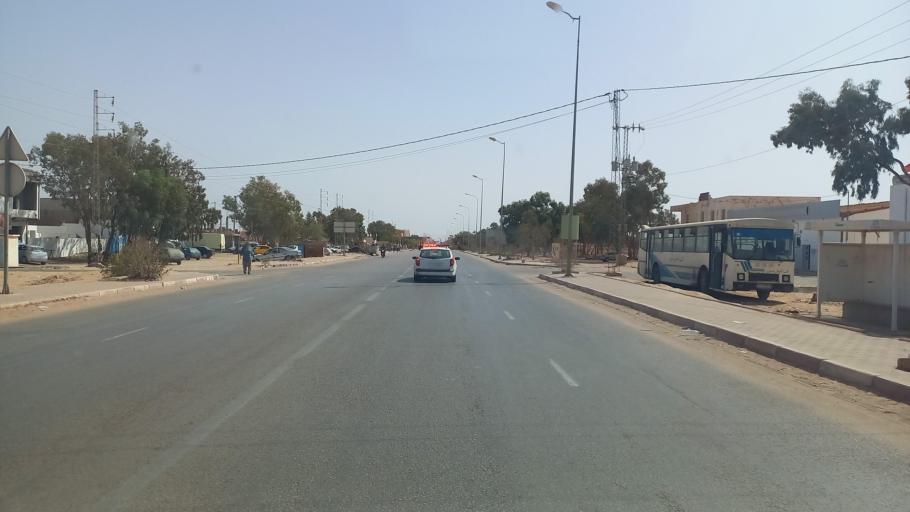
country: TN
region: Madanin
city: Medenine
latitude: 33.3424
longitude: 10.5074
